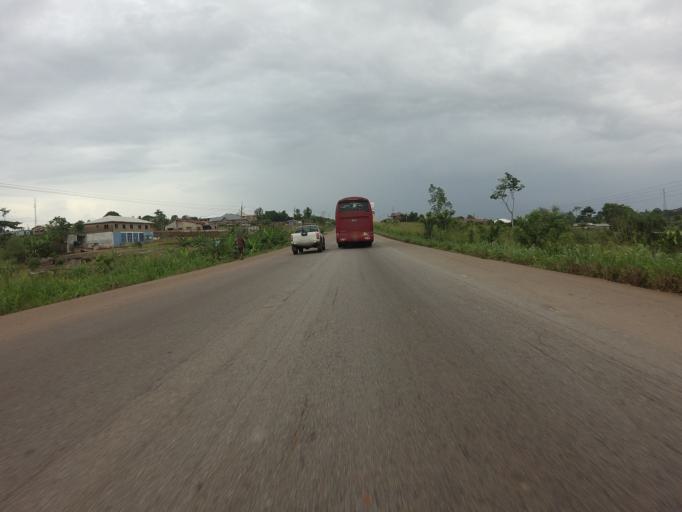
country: GH
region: Ashanti
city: Konongo
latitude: 6.6171
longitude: -1.1789
